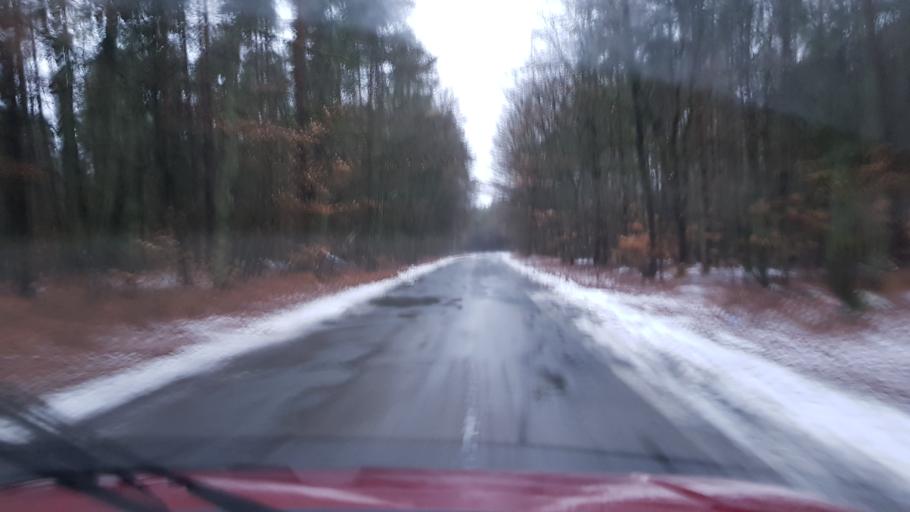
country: PL
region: West Pomeranian Voivodeship
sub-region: Powiat goleniowski
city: Goleniow
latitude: 53.4955
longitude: 14.8844
